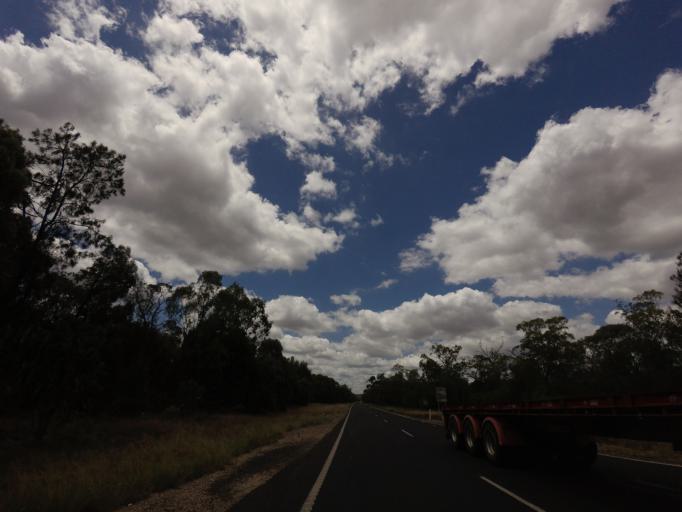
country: AU
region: Queensland
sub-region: Goondiwindi
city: Goondiwindi
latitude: -28.0454
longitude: 150.7901
